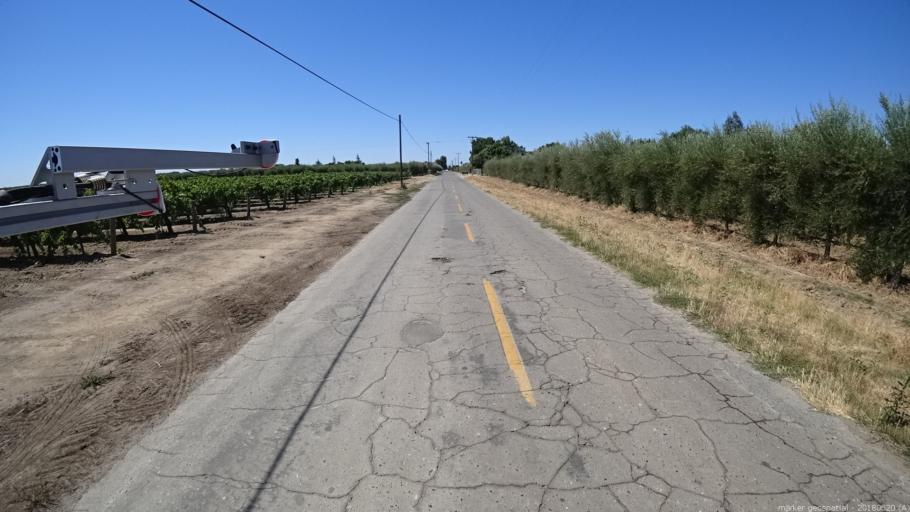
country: US
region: California
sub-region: Madera County
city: Parkwood
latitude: 36.8703
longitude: -120.0104
